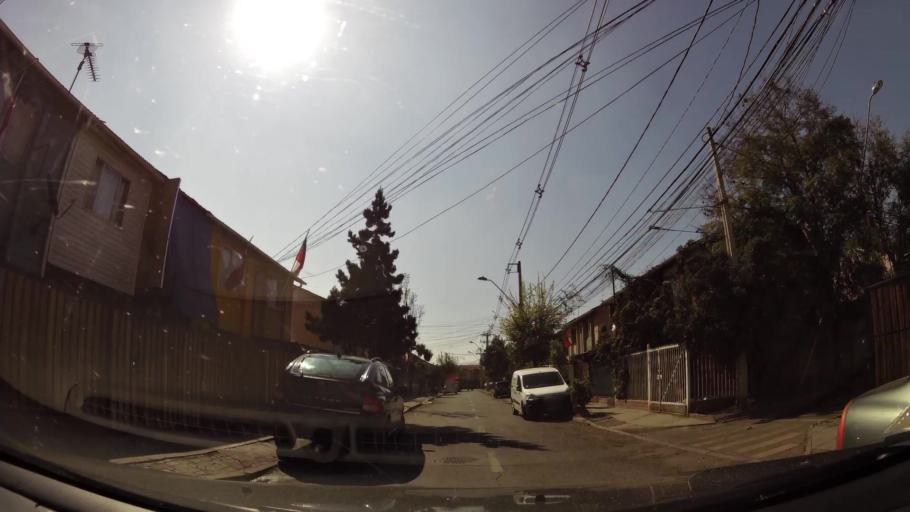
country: CL
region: Santiago Metropolitan
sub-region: Provincia de Santiago
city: Lo Prado
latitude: -33.3583
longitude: -70.7450
